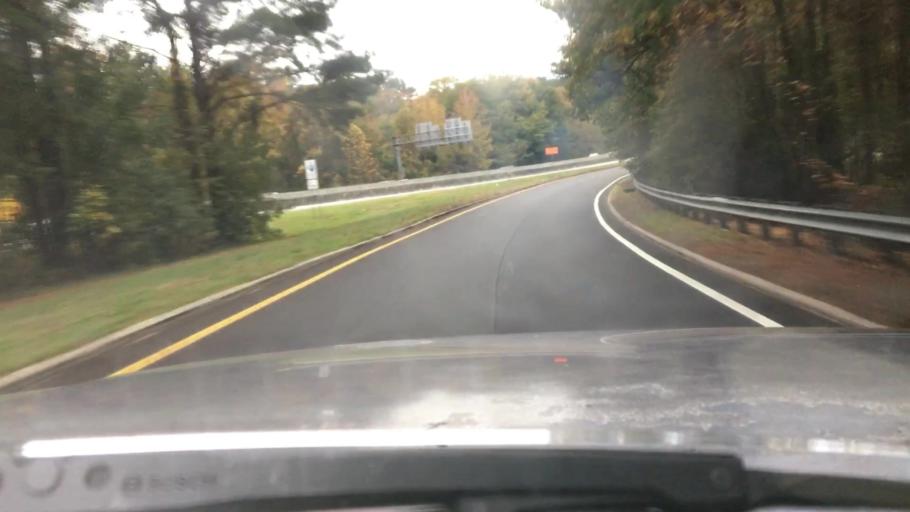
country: US
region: South Carolina
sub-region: Lexington County
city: Saint Andrews
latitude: 34.0363
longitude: -81.1143
